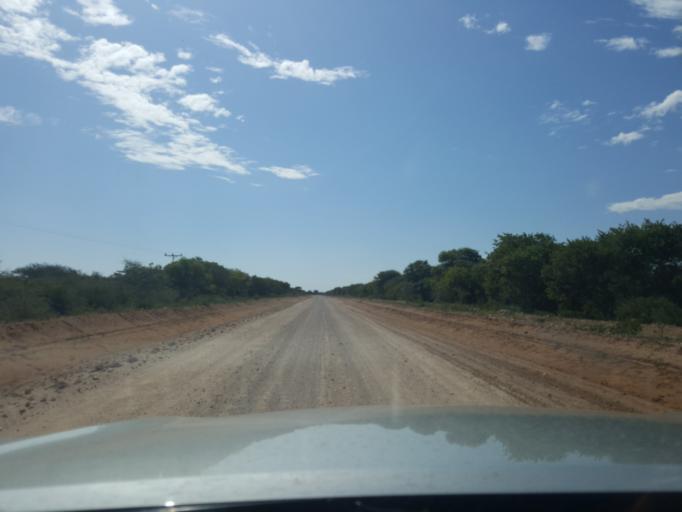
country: BW
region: Kweneng
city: Khudumelapye
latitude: -23.7968
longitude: 24.7976
